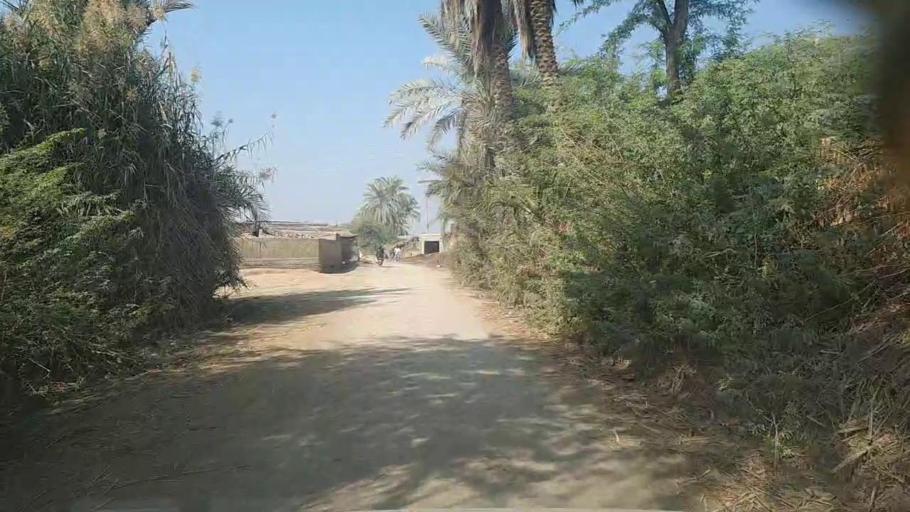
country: PK
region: Sindh
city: Karaundi
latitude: 26.9780
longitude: 68.4498
